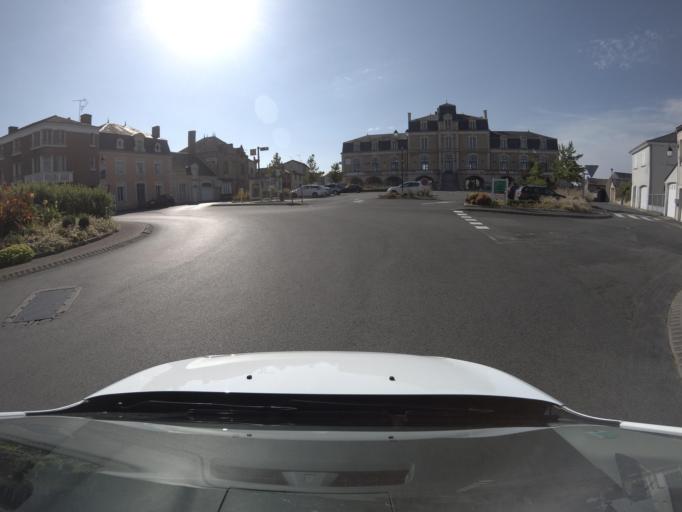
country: FR
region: Poitou-Charentes
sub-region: Departement des Deux-Sevres
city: Argenton-les-Vallees
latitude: 46.9853
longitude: -0.4495
